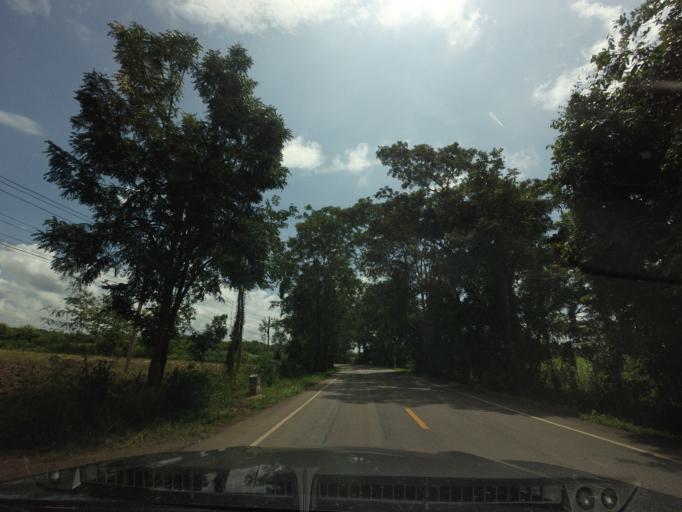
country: TH
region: Nong Khai
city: Pho Tak
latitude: 17.7900
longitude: 102.3607
